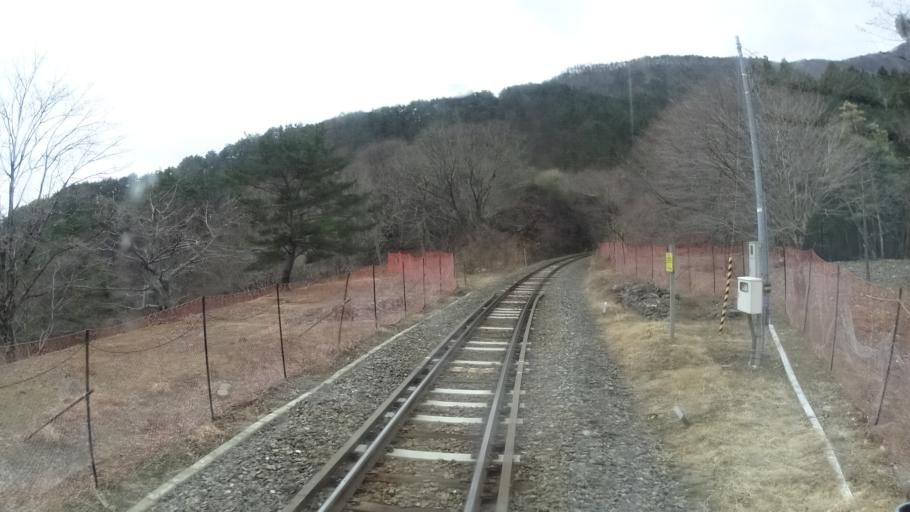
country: JP
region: Iwate
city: Kamaishi
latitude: 39.2549
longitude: 141.7207
